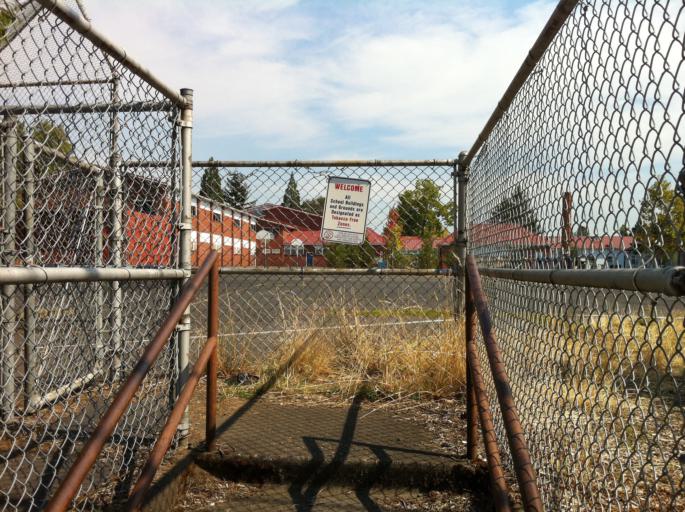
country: US
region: Oregon
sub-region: Clackamas County
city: Lake Oswego
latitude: 45.4641
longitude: -122.6972
